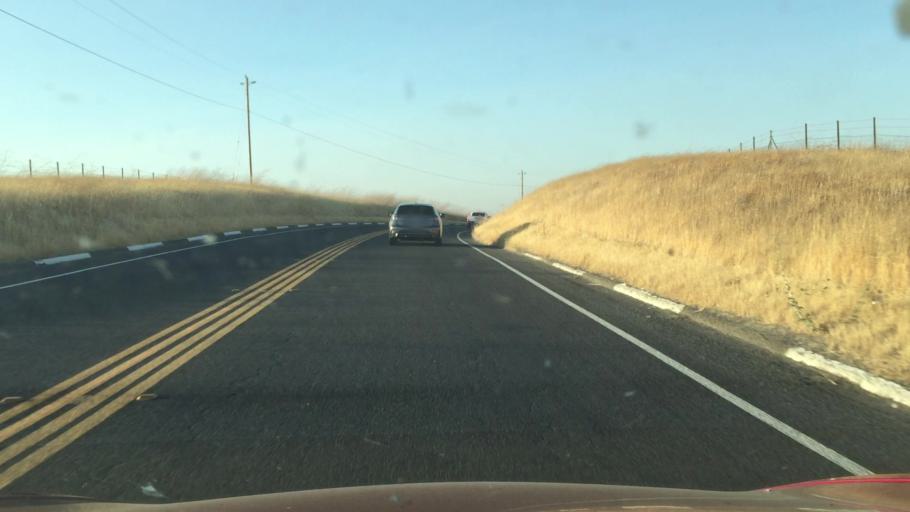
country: US
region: California
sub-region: San Joaquin County
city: Mountain House
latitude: 37.7162
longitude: -121.5391
